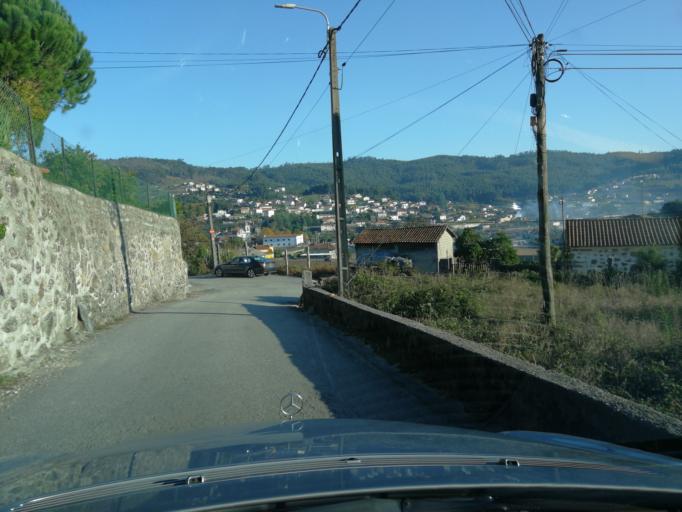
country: PT
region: Braga
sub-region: Braga
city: Oliveira
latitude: 41.4560
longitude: -8.4576
